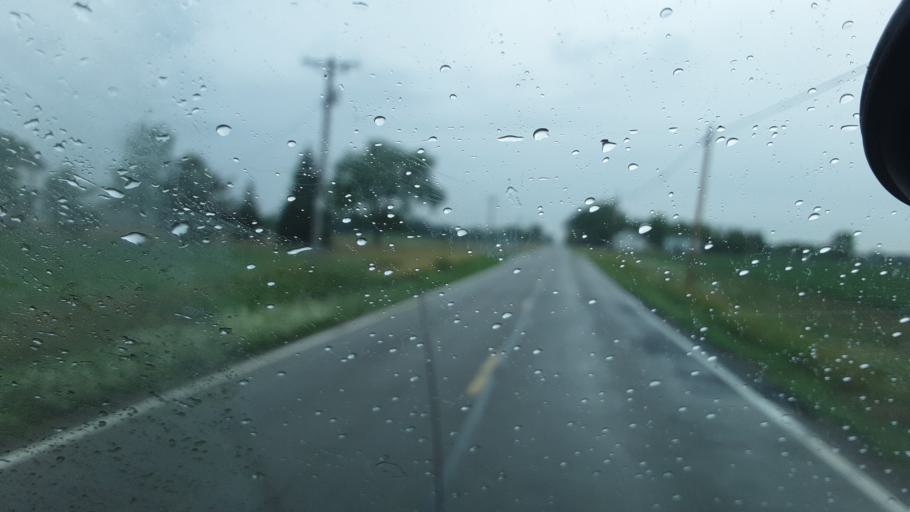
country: US
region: Ohio
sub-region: Williams County
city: Montpelier
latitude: 41.5290
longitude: -84.6129
